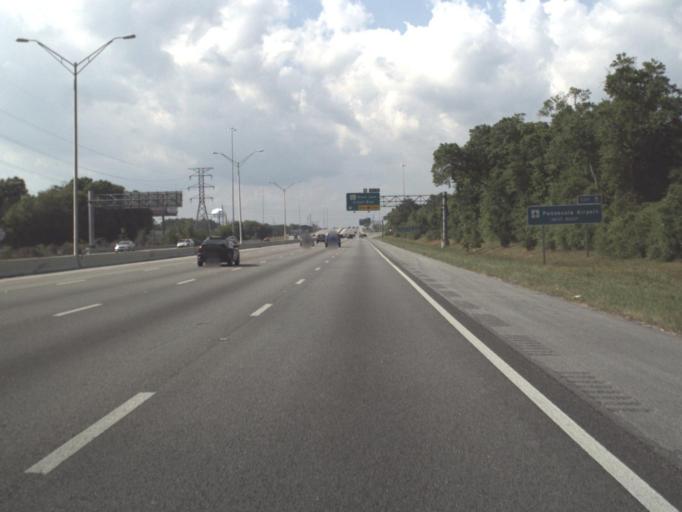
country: US
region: Florida
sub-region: Escambia County
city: Brent
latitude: 30.4629
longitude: -87.2257
